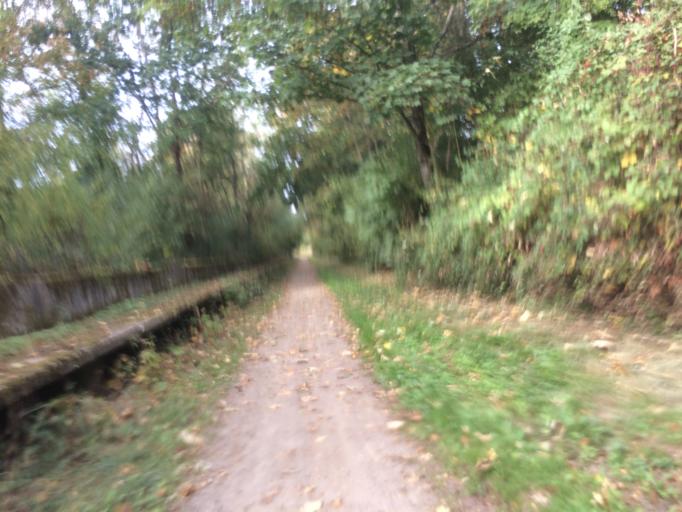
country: FR
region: Ile-de-France
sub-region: Departement de l'Essonne
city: Limours
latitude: 48.6562
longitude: 2.0810
